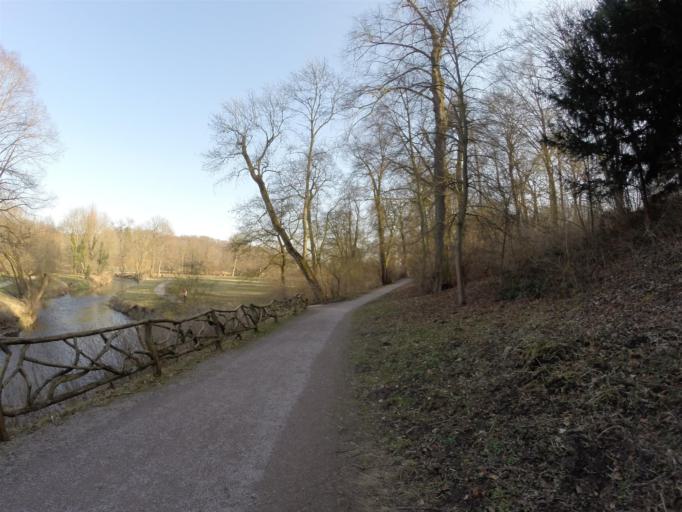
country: DE
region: Thuringia
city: Weimar
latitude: 50.9735
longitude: 11.3343
